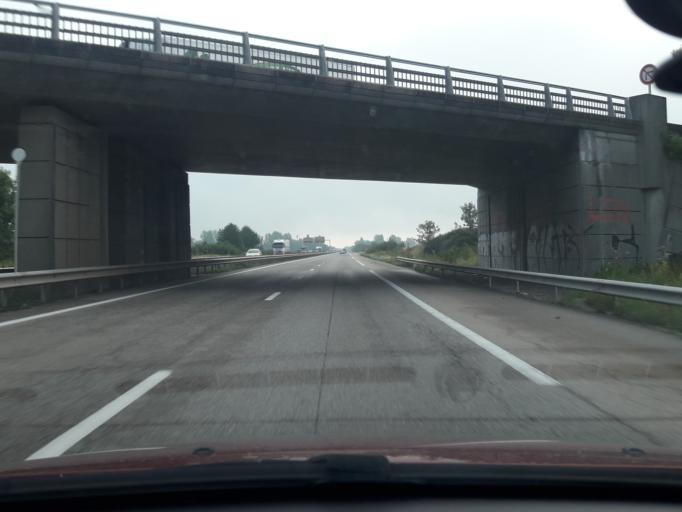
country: FR
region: Alsace
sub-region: Departement du Bas-Rhin
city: Kilstett
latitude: 48.7064
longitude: 7.8550
